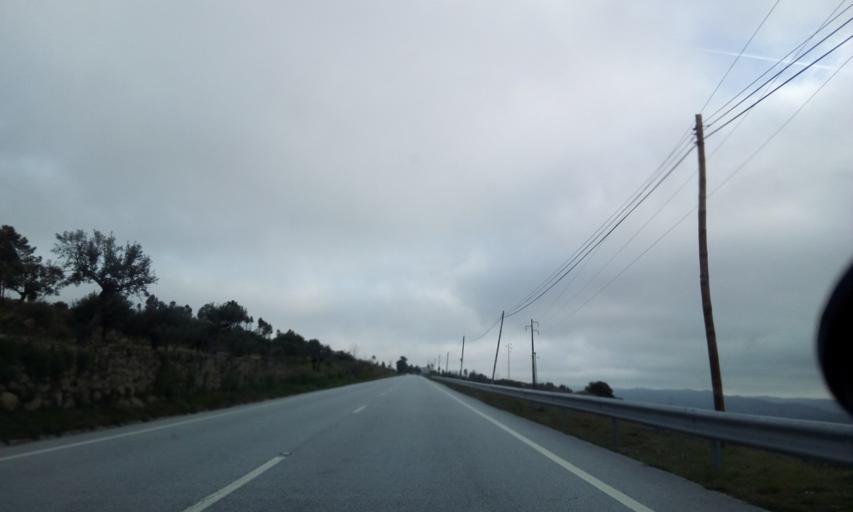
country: PT
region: Guarda
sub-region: Fornos de Algodres
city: Fornos de Algodres
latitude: 40.6604
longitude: -7.4787
